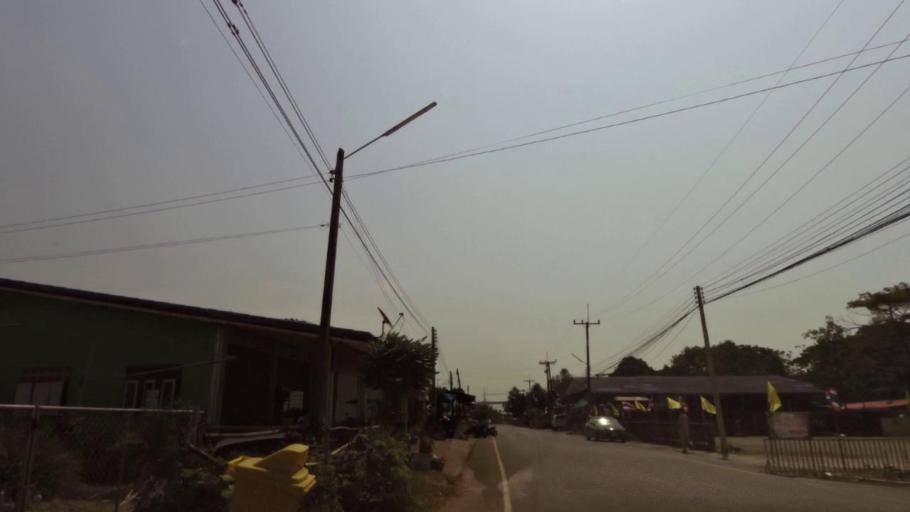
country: TH
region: Chanthaburi
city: Tha Mai
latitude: 12.5313
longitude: 101.9540
